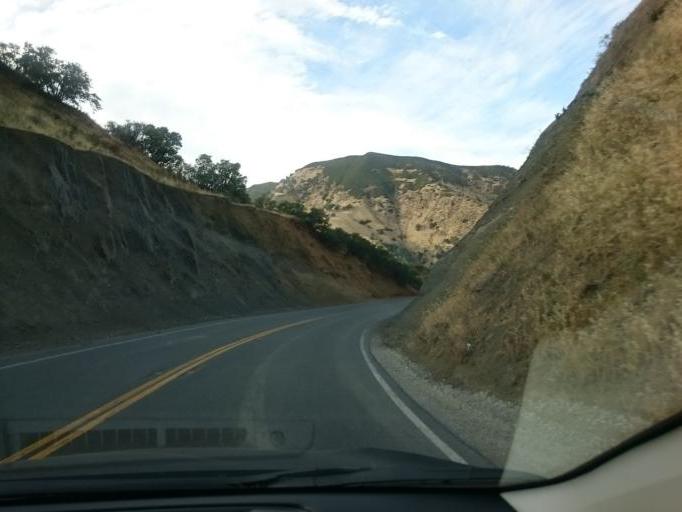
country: US
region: California
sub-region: Yolo County
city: Winters
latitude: 38.5077
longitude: -122.1133
